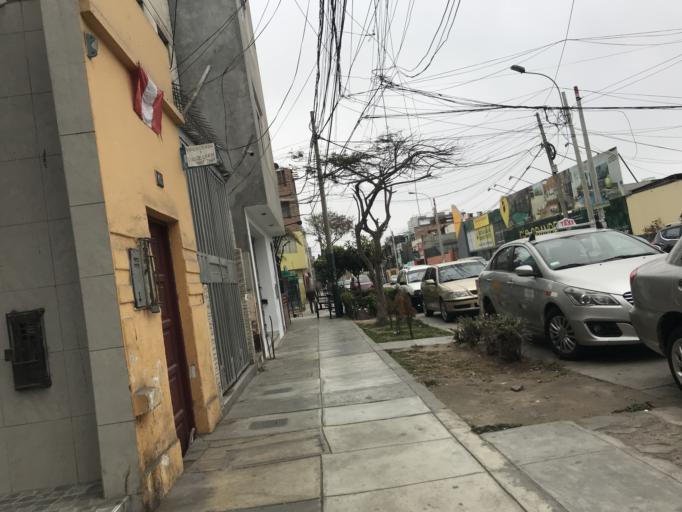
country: PE
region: Lima
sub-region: Lima
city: San Isidro
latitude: -12.0849
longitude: -77.0687
